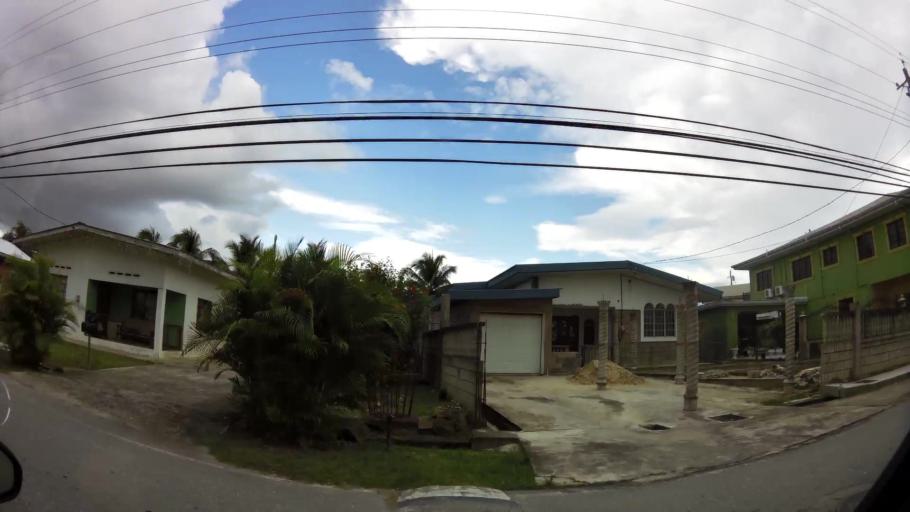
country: TT
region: City of San Fernando
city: Mon Repos
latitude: 10.2547
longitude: -61.4574
